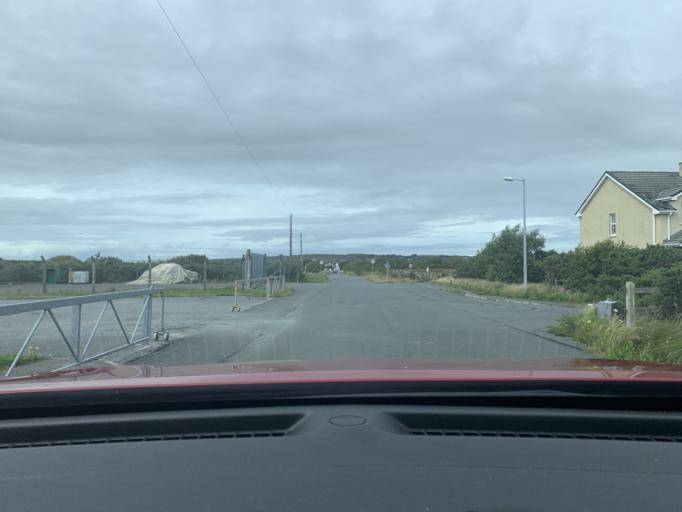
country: IE
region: Ulster
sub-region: County Donegal
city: Dungloe
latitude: 54.9578
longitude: -8.3719
